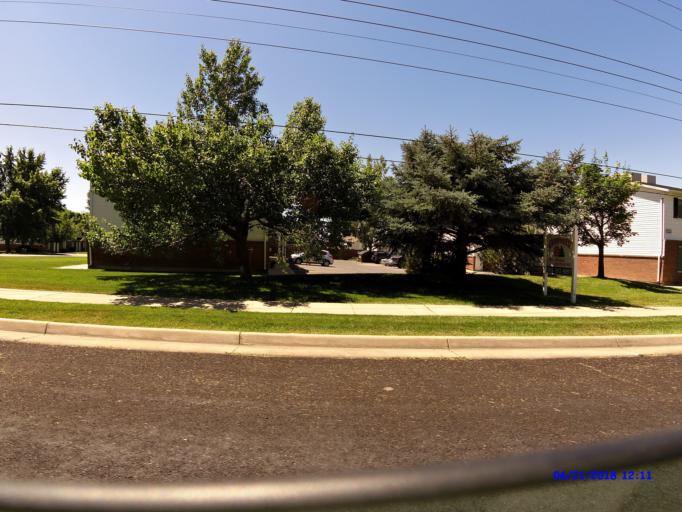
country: US
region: Utah
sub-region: Weber County
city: Harrisville
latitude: 41.2859
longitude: -112.0019
